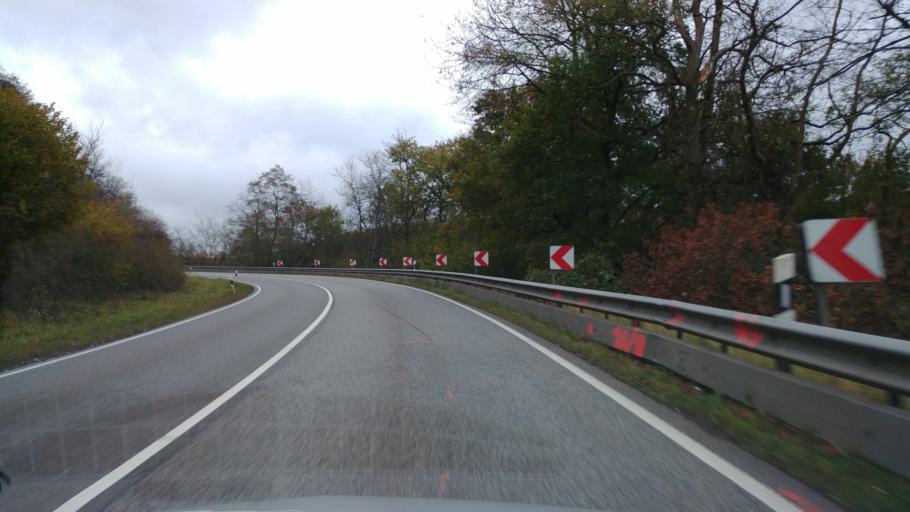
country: DE
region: Rheinland-Pfalz
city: Rorodt
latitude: 49.7812
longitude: 7.0584
